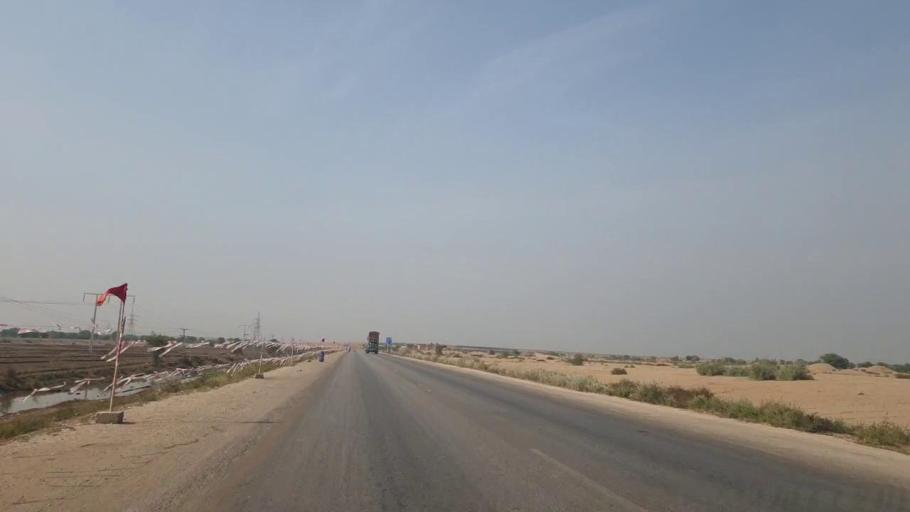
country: PK
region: Sindh
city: Sann
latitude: 26.1495
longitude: 68.0294
